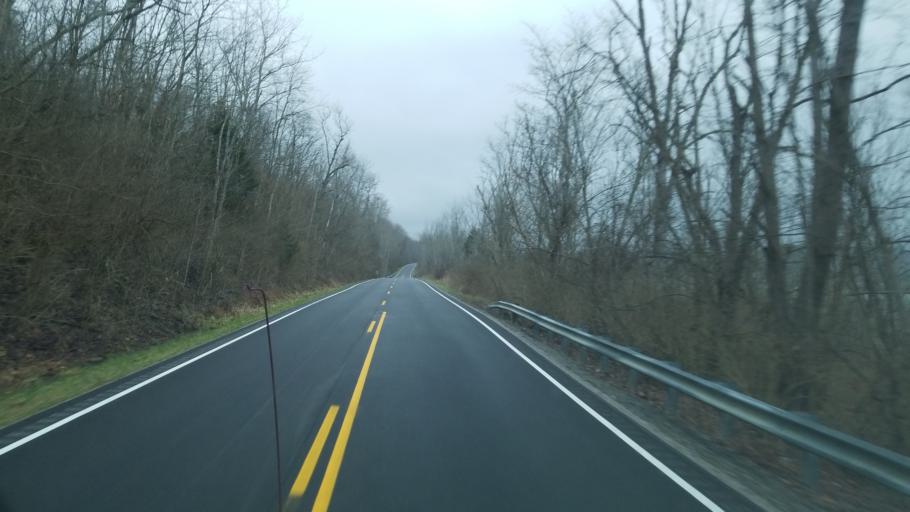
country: US
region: Ohio
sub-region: Brown County
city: Ripley
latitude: 38.7655
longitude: -83.9236
